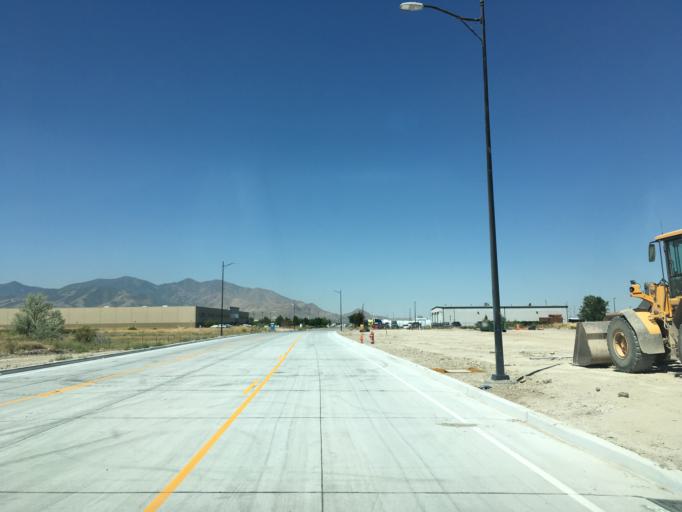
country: US
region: Utah
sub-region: Salt Lake County
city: West Valley City
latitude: 40.7185
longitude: -112.0106
